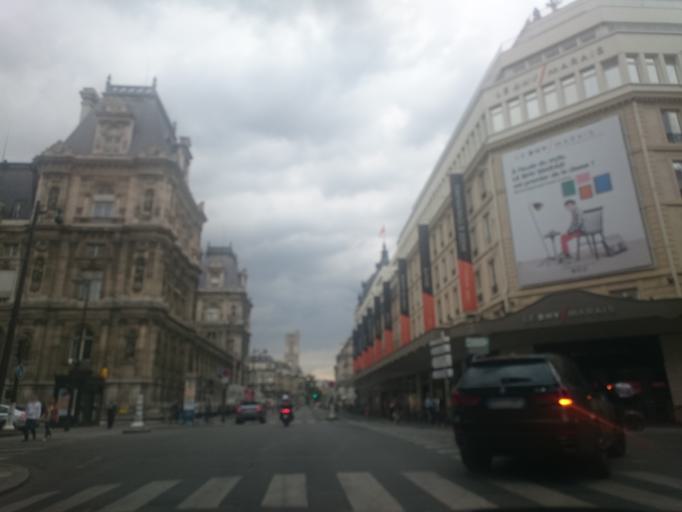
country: FR
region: Ile-de-France
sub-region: Paris
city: Paris
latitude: 48.8569
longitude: 2.3541
